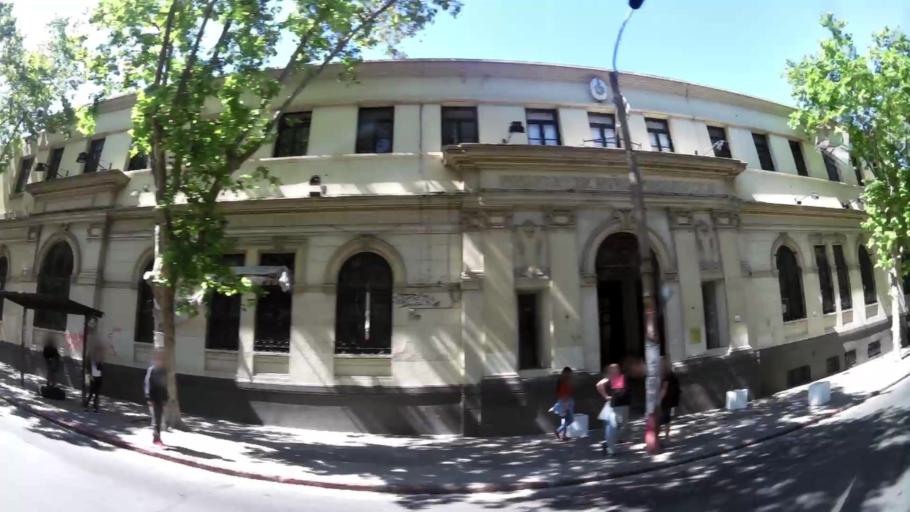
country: UY
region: Montevideo
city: Montevideo
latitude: -34.9119
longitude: -56.1733
